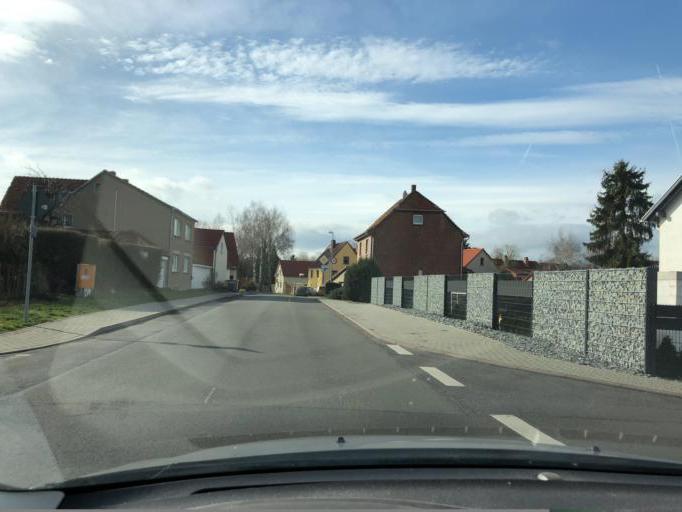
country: DE
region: Thuringia
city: Monchenholzhausen
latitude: 50.9807
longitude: 11.1025
